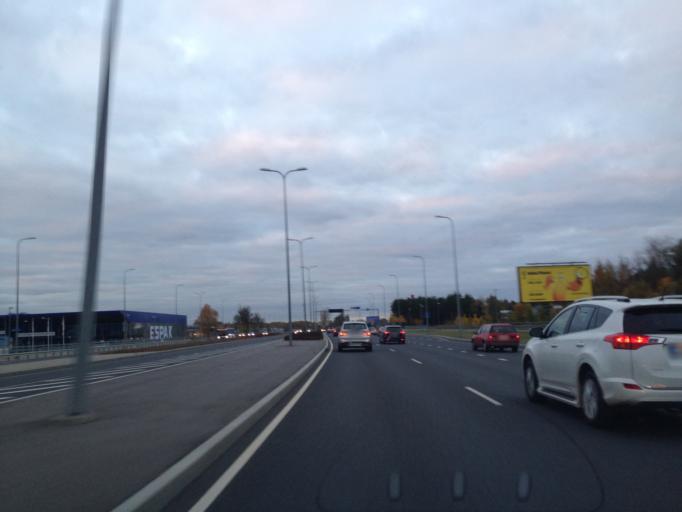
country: EE
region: Harju
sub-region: Tallinna linn
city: Tallinn
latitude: 59.4125
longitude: 24.7578
